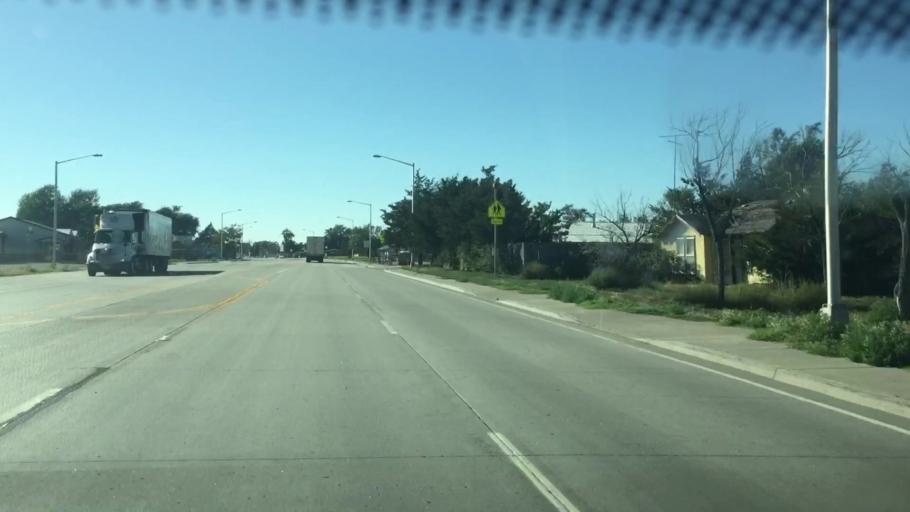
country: US
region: Colorado
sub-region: Kiowa County
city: Eads
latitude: 38.7606
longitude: -102.7876
